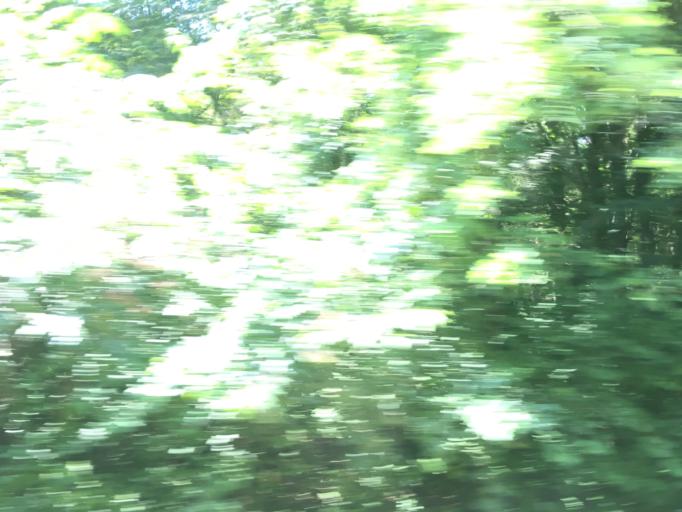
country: SI
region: Metlika
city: Metlika
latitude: 45.5892
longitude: 15.3444
